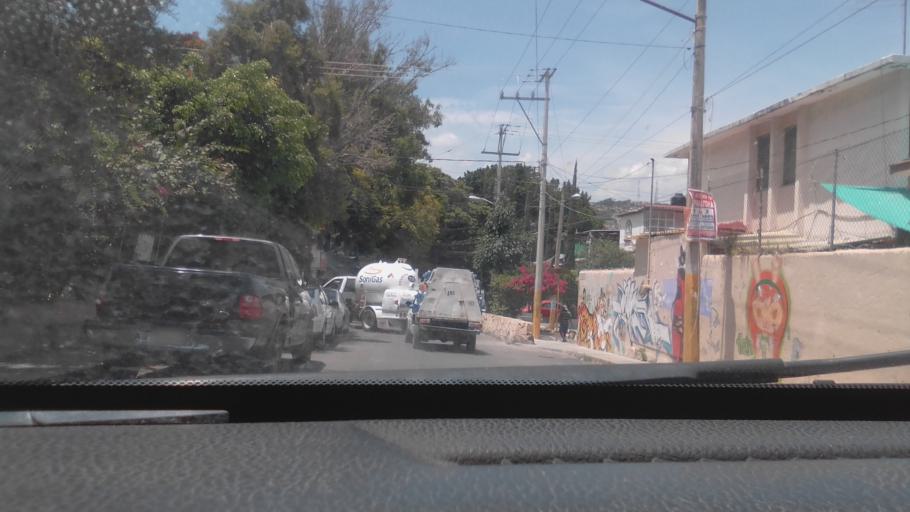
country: MX
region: Guerrero
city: Chilpancingo de los Bravos
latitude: 17.5592
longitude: -99.5045
